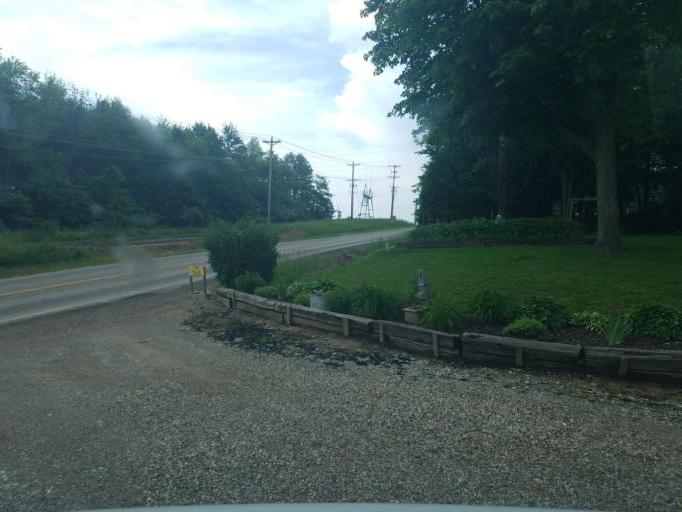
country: US
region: Ohio
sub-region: Knox County
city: Oak Hill
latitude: 40.3328
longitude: -82.2411
